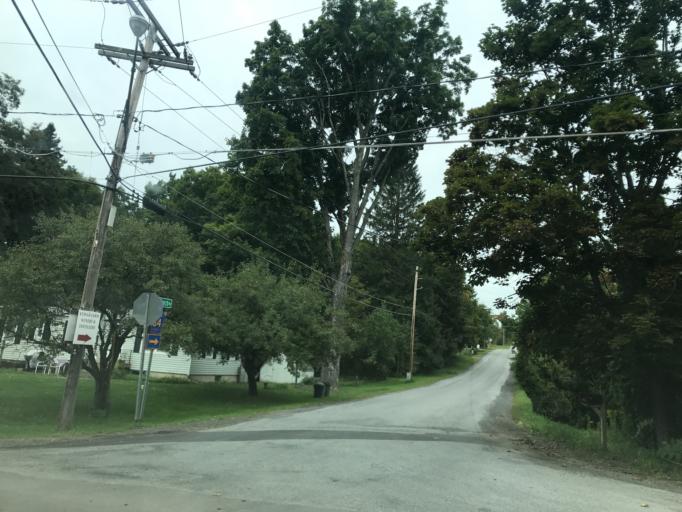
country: US
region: New York
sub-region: Otsego County
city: Worcester
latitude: 42.5451
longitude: -74.6648
